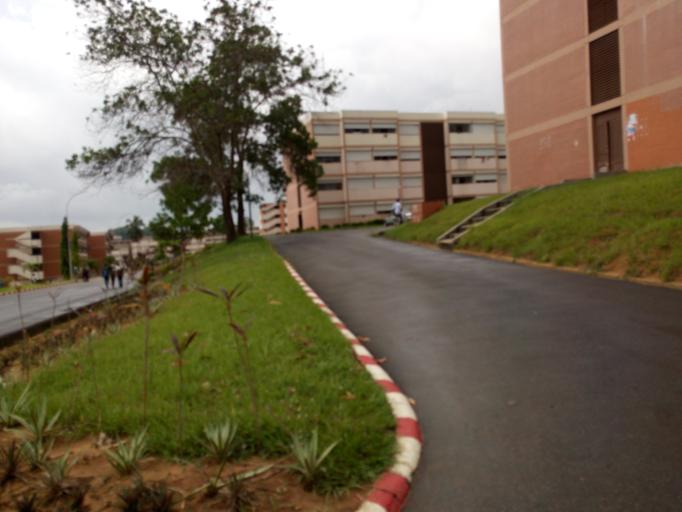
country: CI
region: Lagunes
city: Abidjan
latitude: 5.3388
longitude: -3.9901
